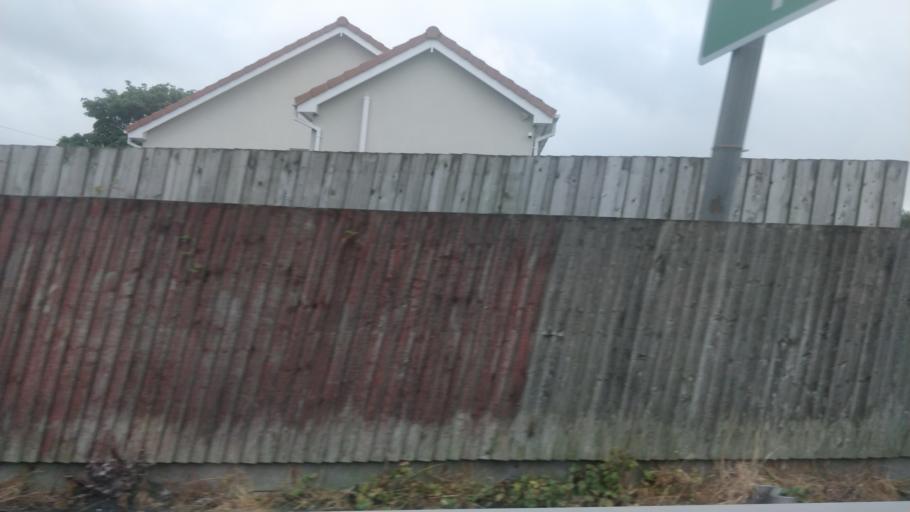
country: GB
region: England
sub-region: Sefton
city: Maghull
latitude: 53.4981
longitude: -2.9479
